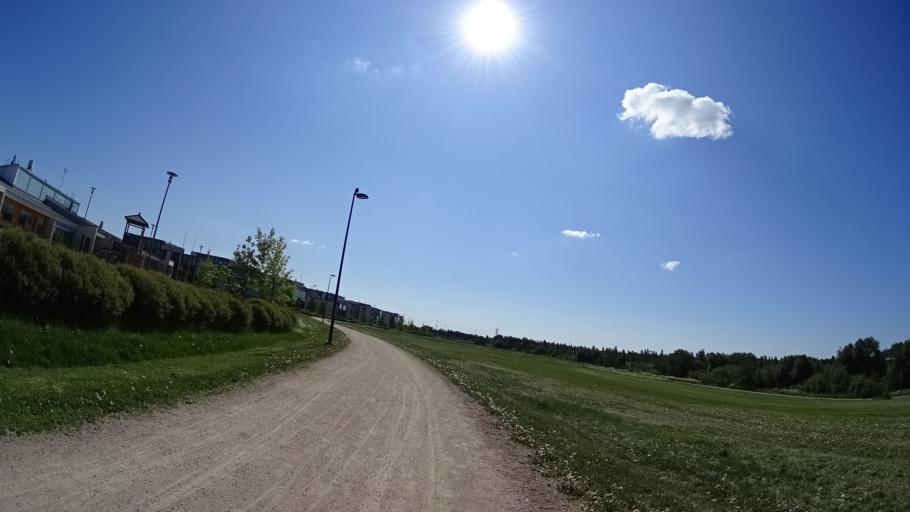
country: FI
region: Uusimaa
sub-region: Helsinki
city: Vantaa
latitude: 60.2689
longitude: 24.9617
